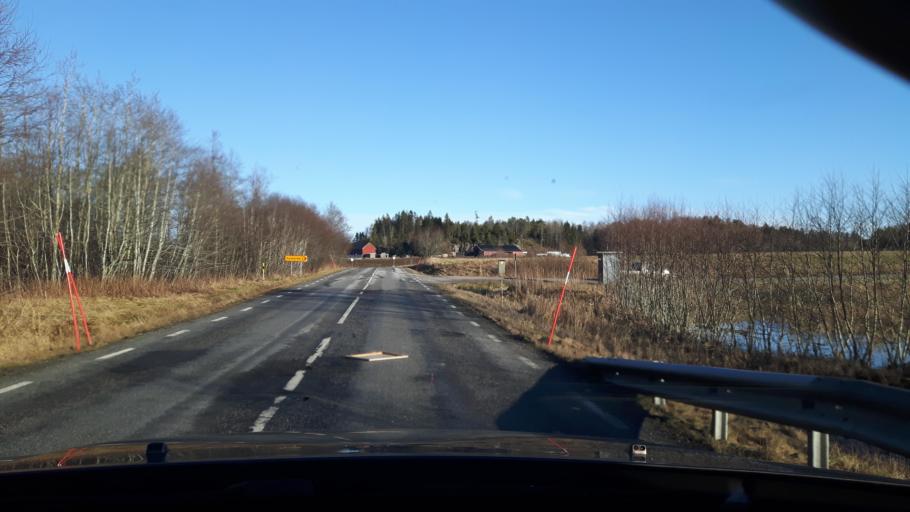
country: SE
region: Vaestra Goetaland
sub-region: Munkedals Kommun
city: Munkedal
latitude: 58.5952
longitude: 11.7488
